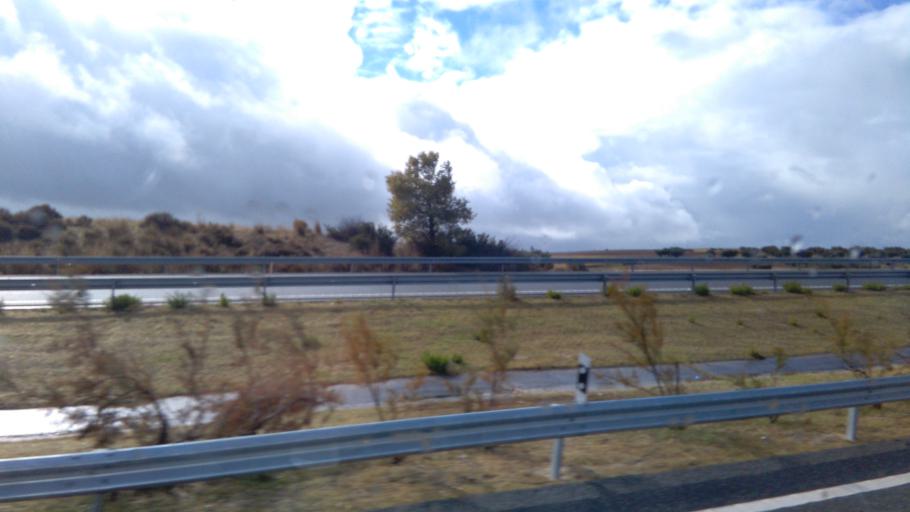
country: ES
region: Madrid
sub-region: Provincia de Madrid
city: El Alamo
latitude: 40.2595
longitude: -3.9837
